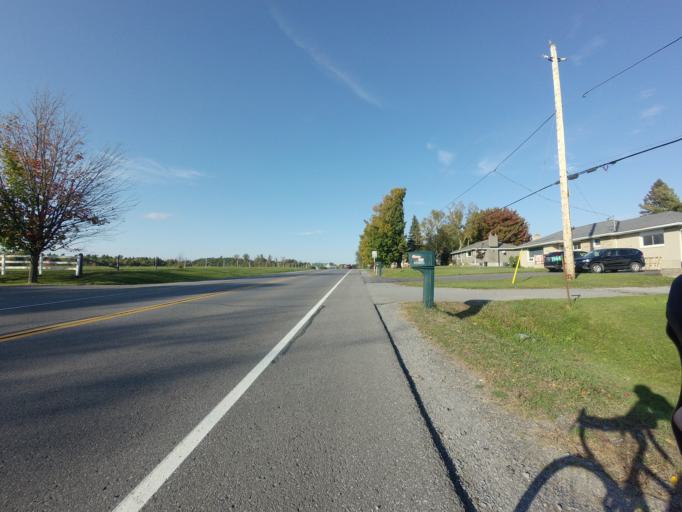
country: CA
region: Ontario
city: Kingston
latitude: 44.3066
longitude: -76.4653
